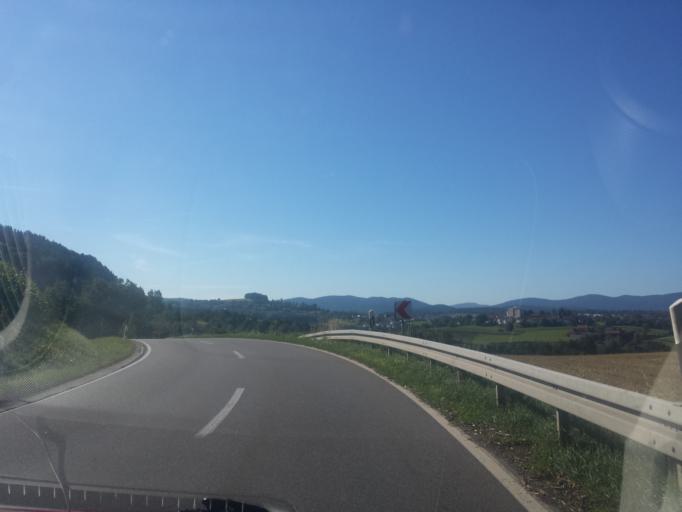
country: DE
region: Bavaria
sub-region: Lower Bavaria
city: Viechtach
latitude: 49.0979
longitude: 12.8868
